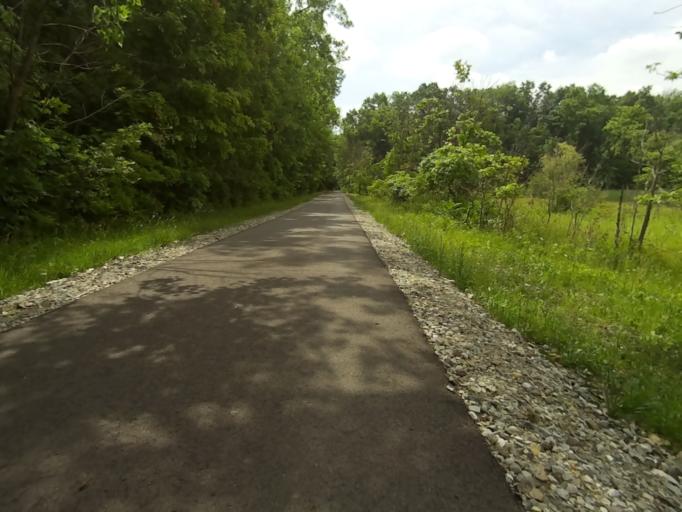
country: US
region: Ohio
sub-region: Summit County
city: Boston Heights
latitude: 41.2537
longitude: -81.5176
